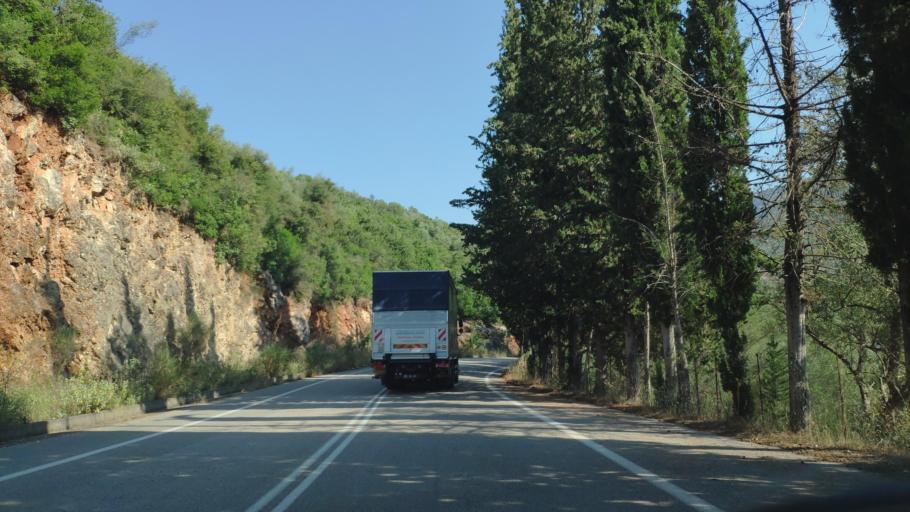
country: GR
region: West Greece
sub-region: Nomos Aitolias kai Akarnanias
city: Stanos
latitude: 38.7740
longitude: 21.1485
